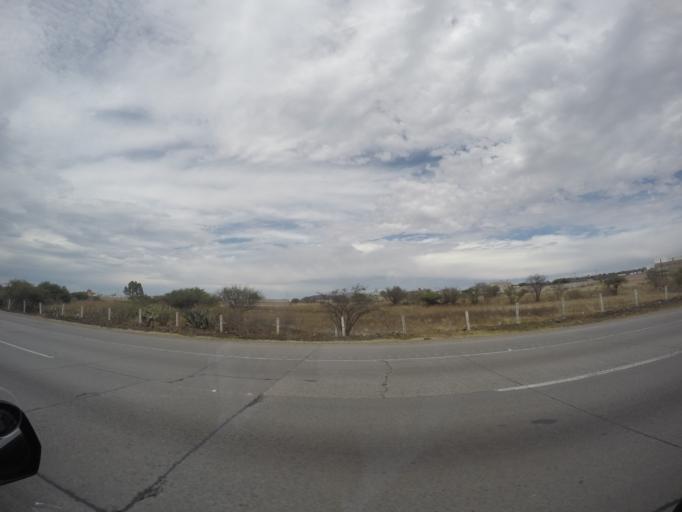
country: MX
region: Queretaro
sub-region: San Juan del Rio
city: Paso de Mata
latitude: 20.3518
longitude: -99.9543
